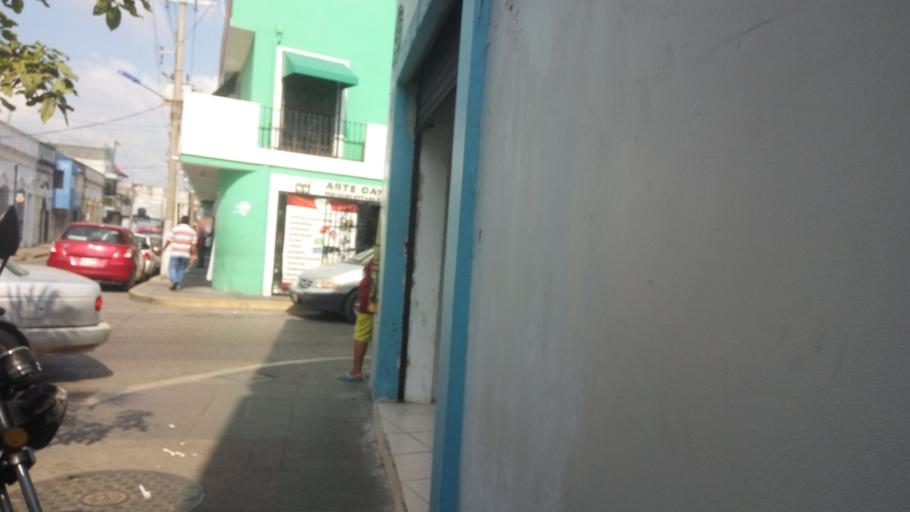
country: MX
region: Tabasco
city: Villahermosa
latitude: 17.9908
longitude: -92.9192
